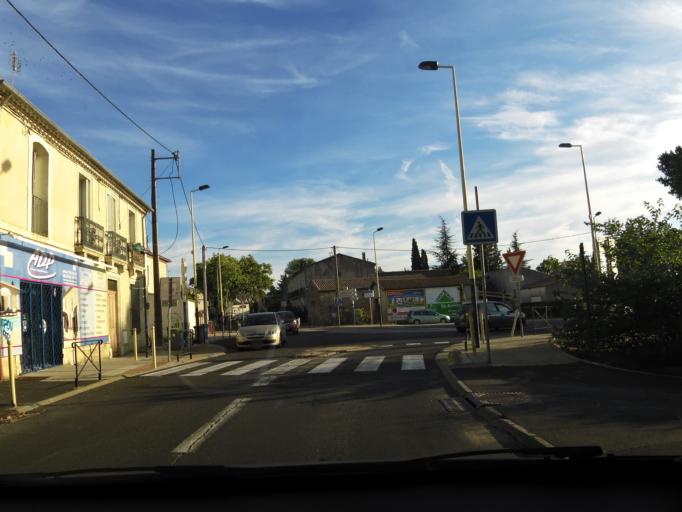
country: FR
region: Languedoc-Roussillon
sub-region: Departement de l'Herault
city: Prades-le-Lez
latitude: 43.7010
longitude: 3.8626
